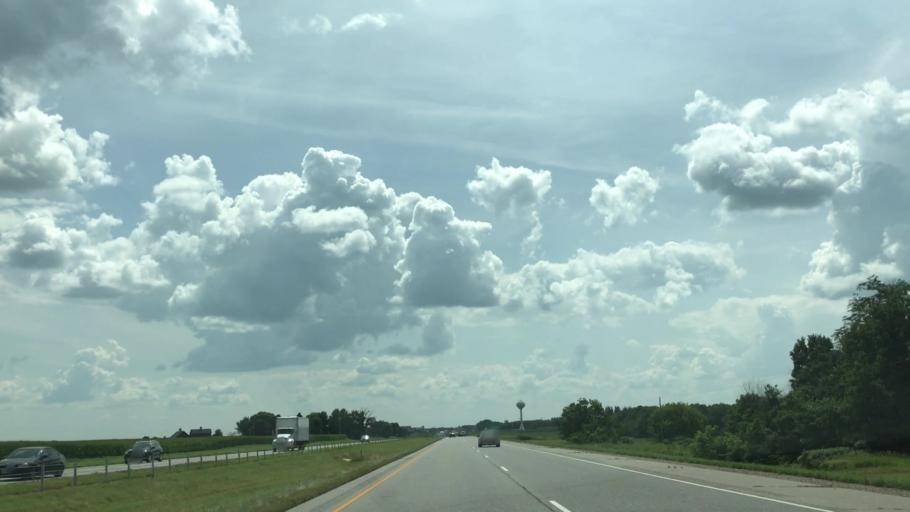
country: US
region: Minnesota
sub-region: Le Sueur County
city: Le Sueur
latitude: 44.5108
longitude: -93.8546
